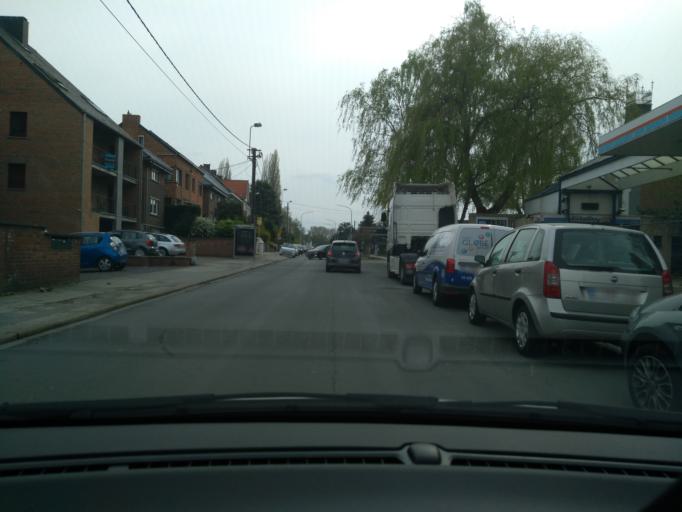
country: BE
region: Wallonia
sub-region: Province du Brabant Wallon
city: Nivelles
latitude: 50.5932
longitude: 4.3178
